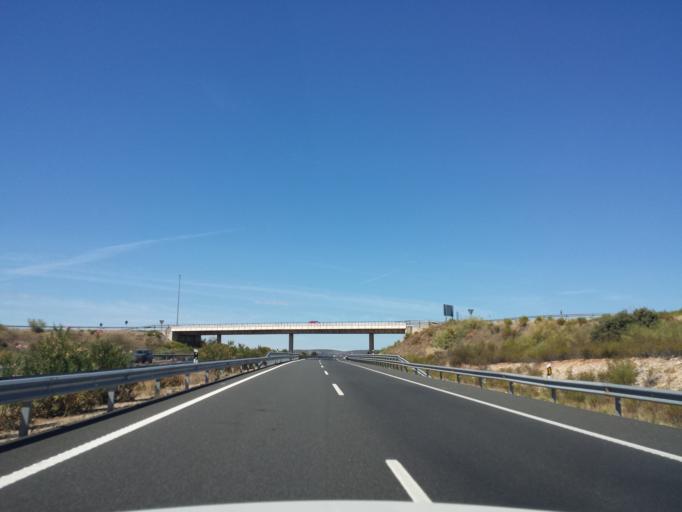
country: ES
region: Extremadura
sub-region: Provincia de Caceres
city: Almaraz
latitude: 39.7902
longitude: -5.6966
